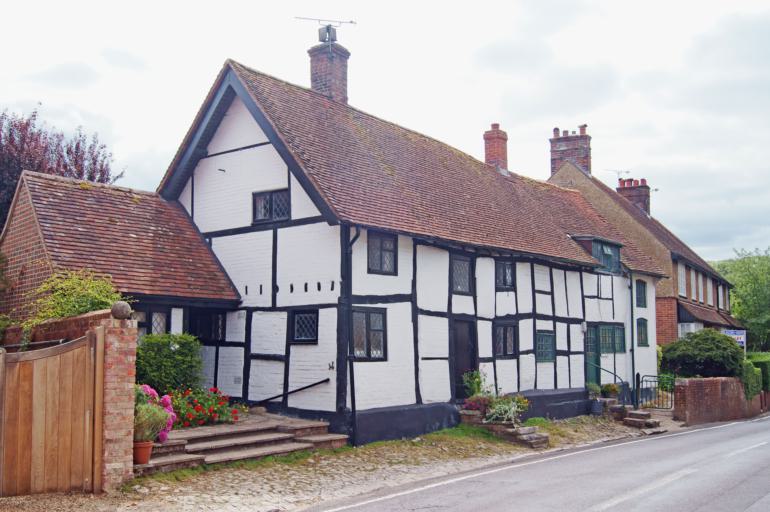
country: GB
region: England
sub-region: Hampshire
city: Petersfield
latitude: 50.9689
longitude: -0.8840
